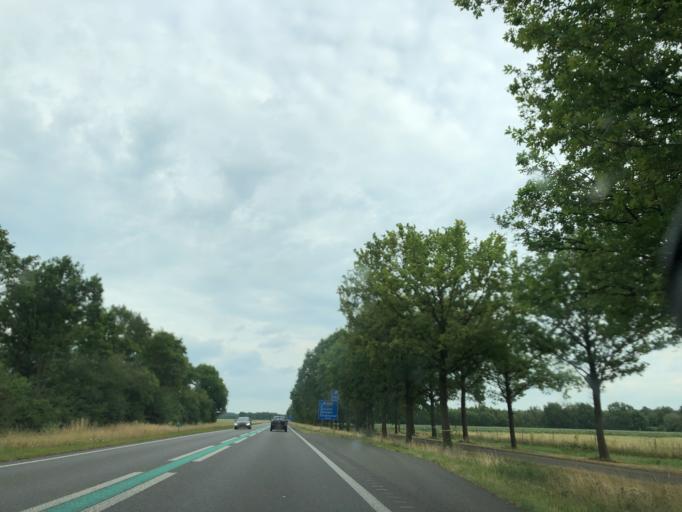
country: NL
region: Drenthe
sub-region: Gemeente Borger-Odoorn
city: Borger
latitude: 52.9843
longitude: 6.7685
